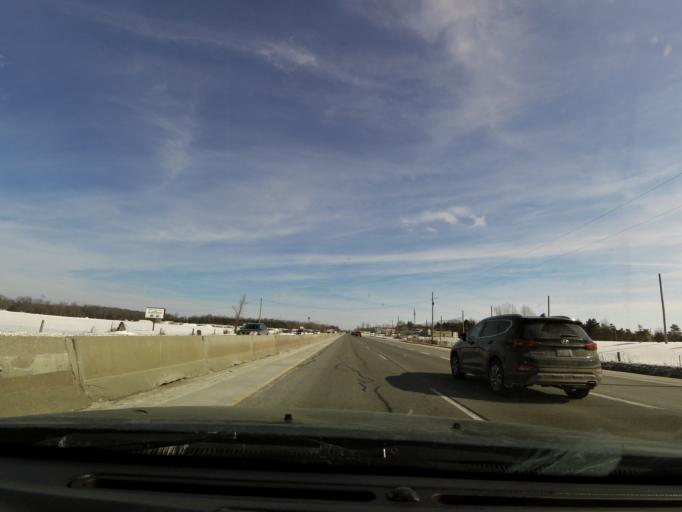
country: CA
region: Ontario
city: Orillia
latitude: 44.4997
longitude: -79.4915
